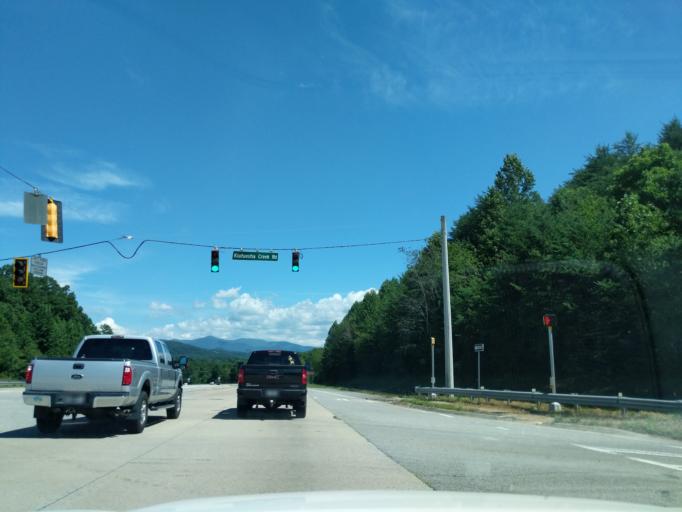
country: US
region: Georgia
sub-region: Union County
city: Blairsville
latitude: 34.8606
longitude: -84.0048
